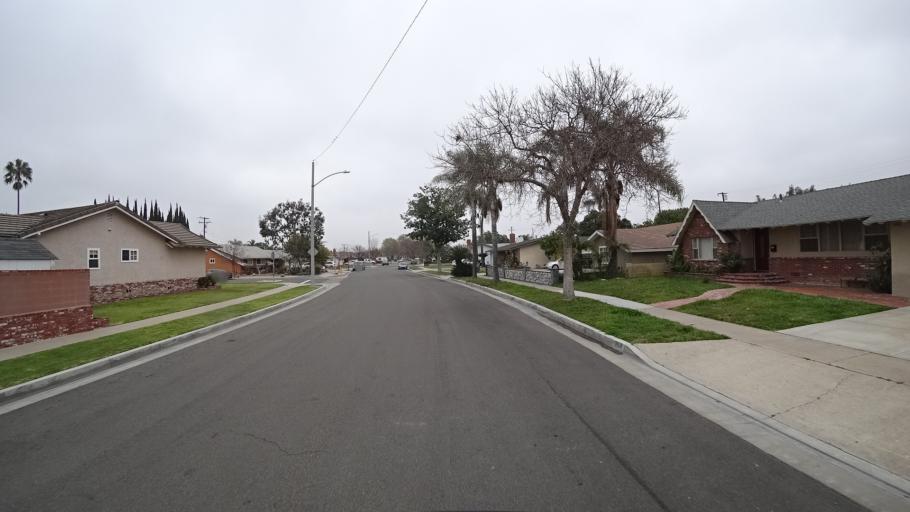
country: US
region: California
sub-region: Orange County
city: Stanton
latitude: 33.8187
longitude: -118.0086
